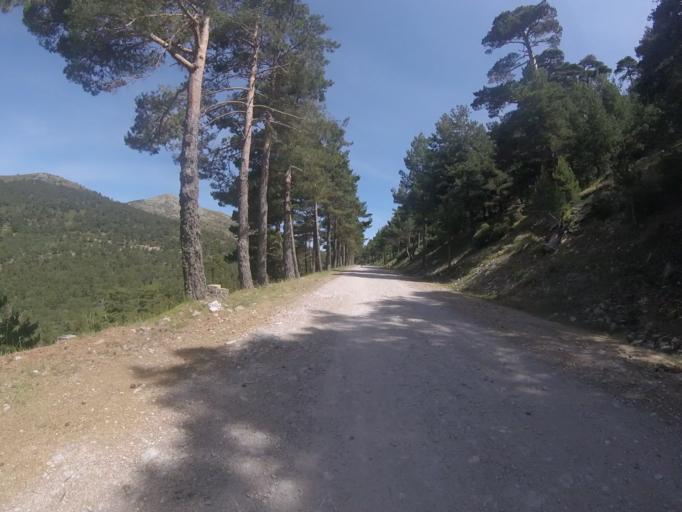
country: ES
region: Madrid
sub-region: Provincia de Madrid
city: Cercedilla
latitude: 40.7889
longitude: -4.0591
